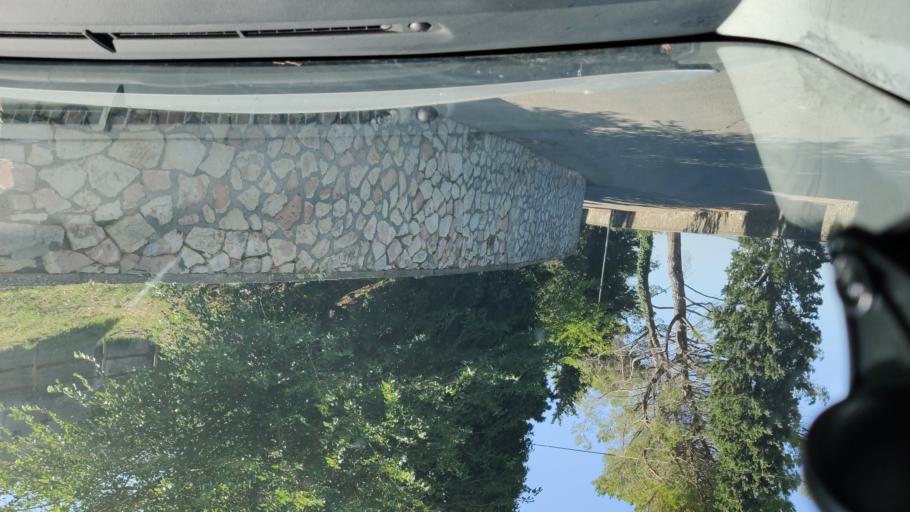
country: IT
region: Umbria
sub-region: Provincia di Terni
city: Amelia
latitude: 42.5131
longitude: 12.4273
